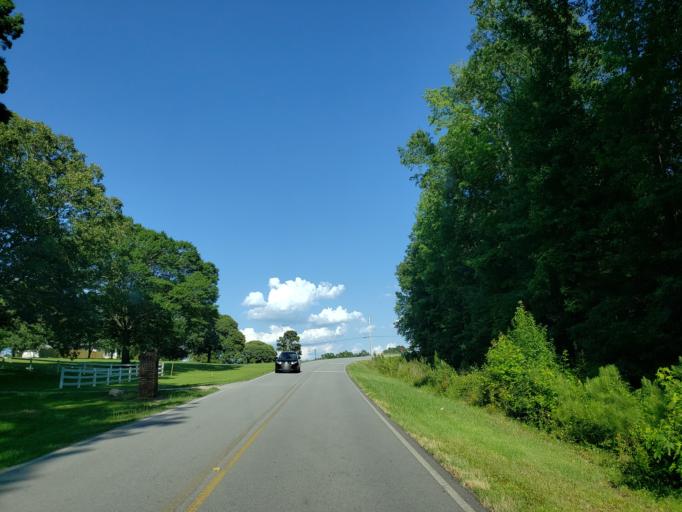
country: US
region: Georgia
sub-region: Haralson County
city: Bremen
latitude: 33.6843
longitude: -85.0907
